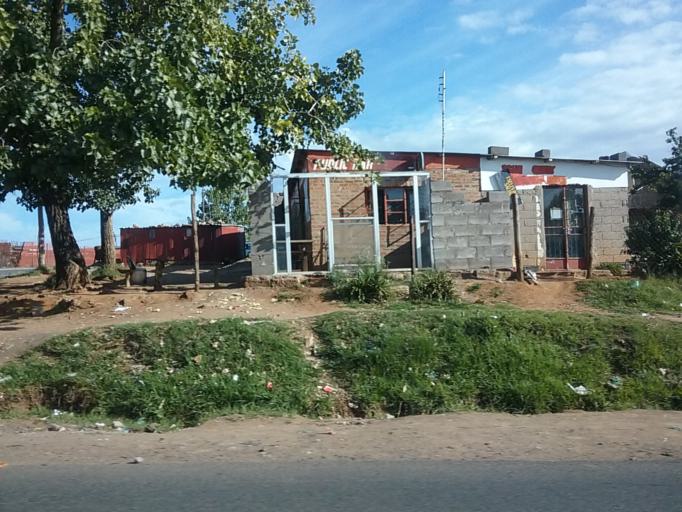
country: LS
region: Berea
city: Teyateyaneng
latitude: -29.1527
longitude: 27.7435
